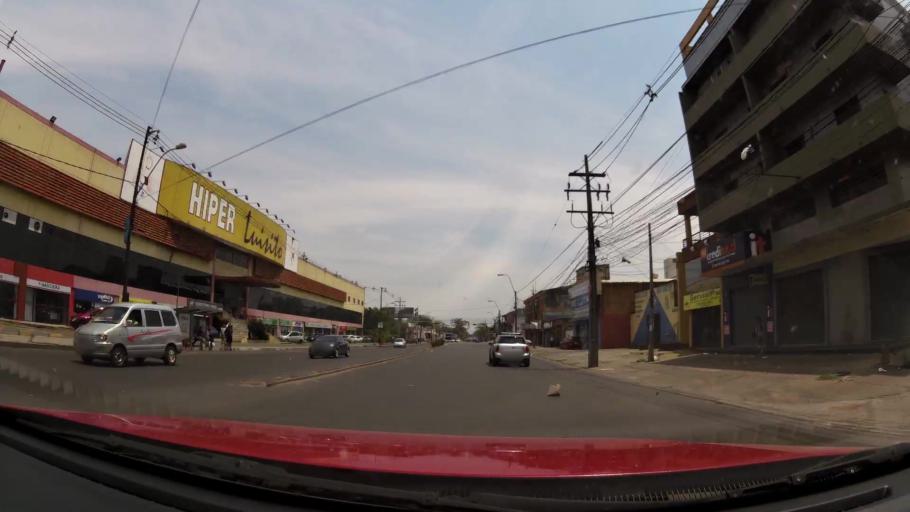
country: PY
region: Central
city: Lambare
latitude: -25.3151
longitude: -57.5779
